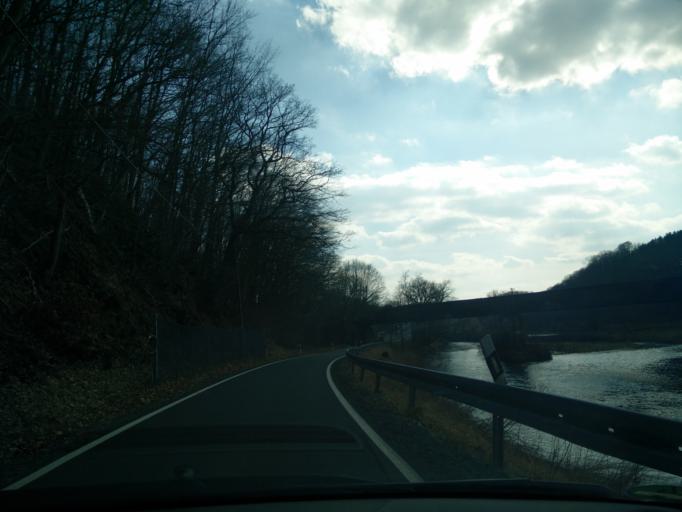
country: DE
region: Saxony
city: Colditz
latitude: 51.1055
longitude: 12.8096
